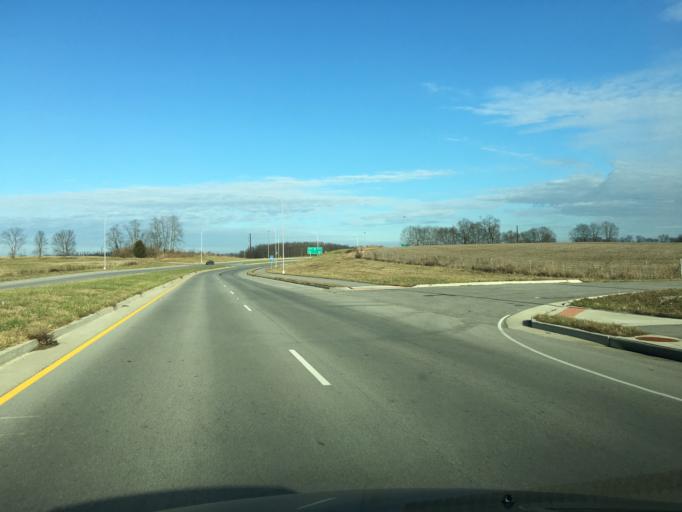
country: US
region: Kentucky
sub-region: Scott County
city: Georgetown
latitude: 38.2396
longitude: -84.5510
